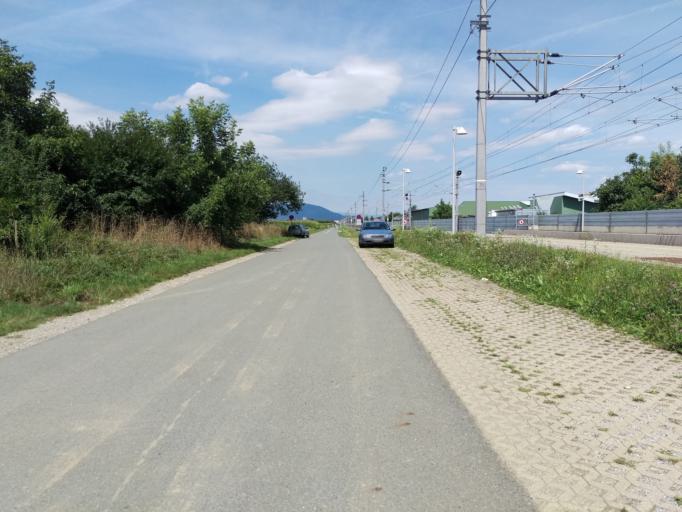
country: AT
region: Styria
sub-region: Politischer Bezirk Graz-Umgebung
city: Feldkirchen bei Graz
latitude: 46.9985
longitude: 15.4490
